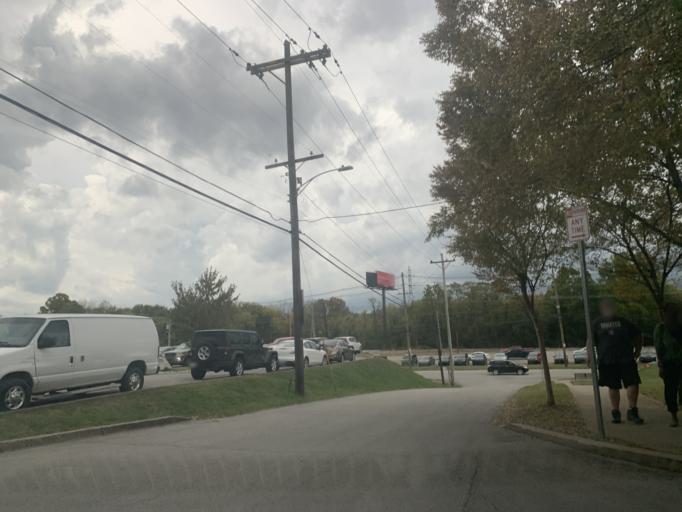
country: US
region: Indiana
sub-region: Clark County
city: Jeffersonville
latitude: 38.2624
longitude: -85.7138
